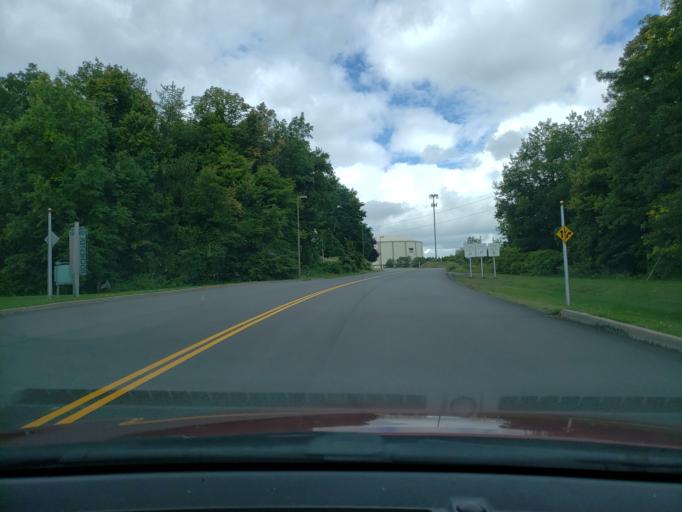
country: US
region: New York
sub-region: Monroe County
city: North Gates
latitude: 43.1567
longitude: -77.7415
